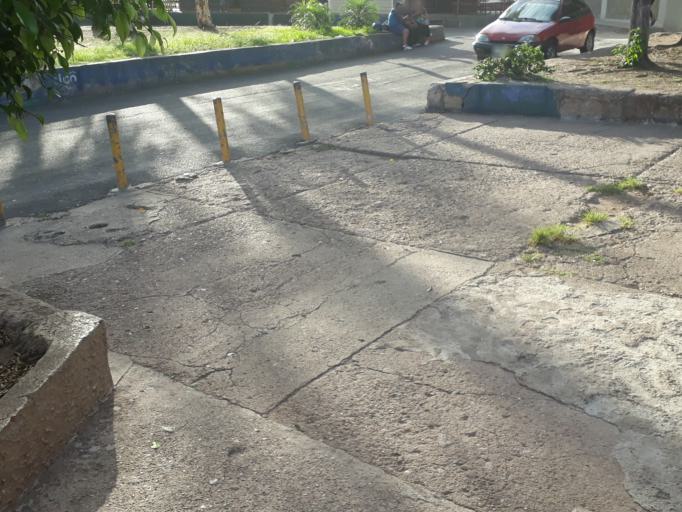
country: HN
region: Francisco Morazan
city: Tegucigalpa
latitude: 14.0908
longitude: -87.1636
